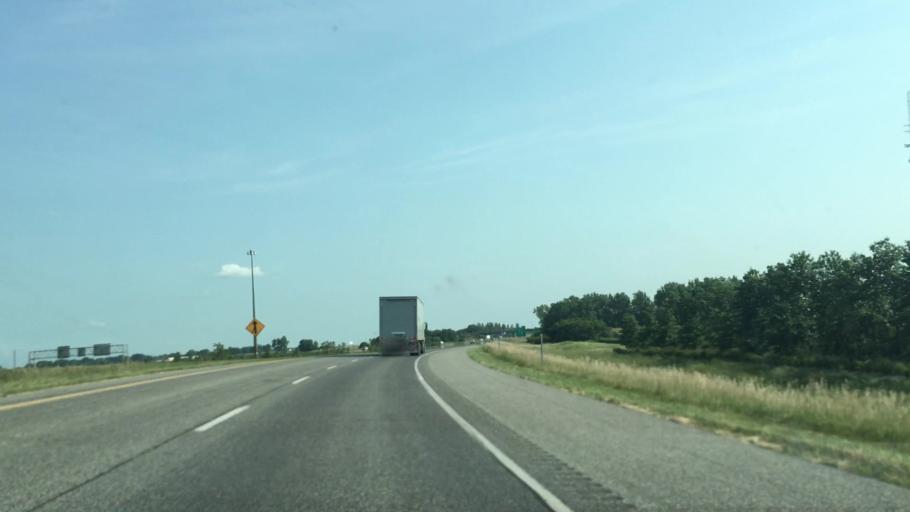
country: US
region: Iowa
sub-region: Scott County
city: Walcott
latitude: 41.5998
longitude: -90.6773
